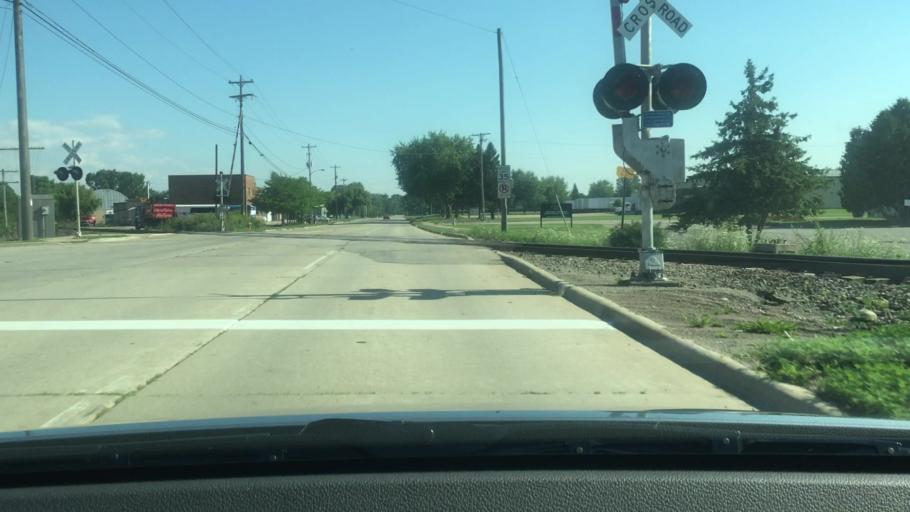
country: US
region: Wisconsin
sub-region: Winnebago County
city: Oshkosh
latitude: 43.9867
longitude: -88.5425
